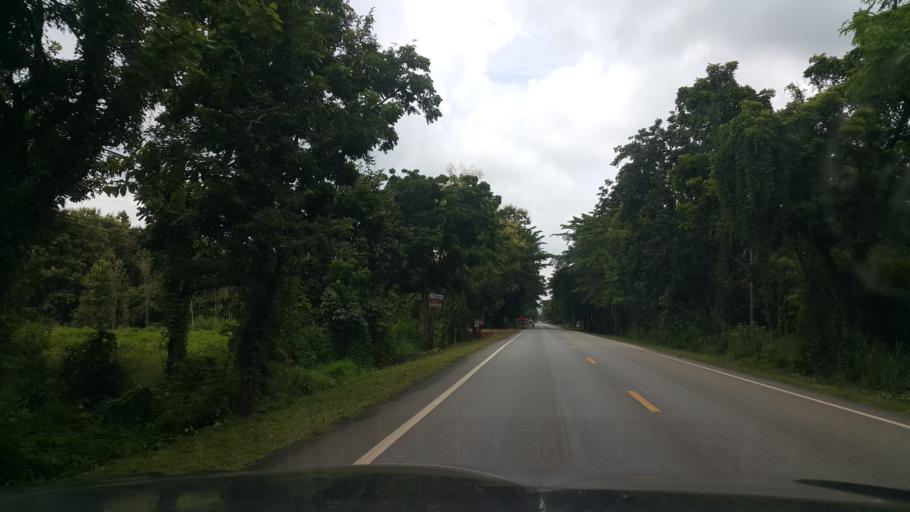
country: TH
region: Uttaradit
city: Lap Lae
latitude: 17.5838
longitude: 99.9662
